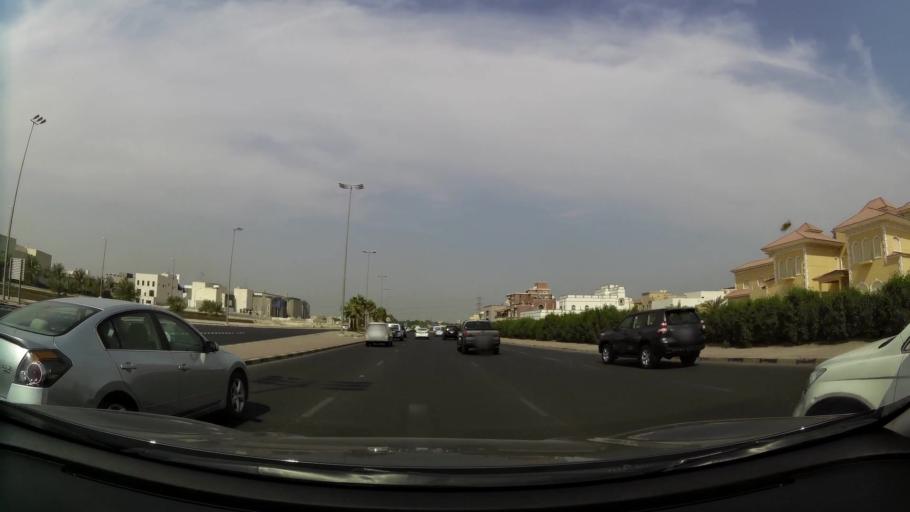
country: KW
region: Al Farwaniyah
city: Janub as Surrah
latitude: 29.2987
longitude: 48.0024
